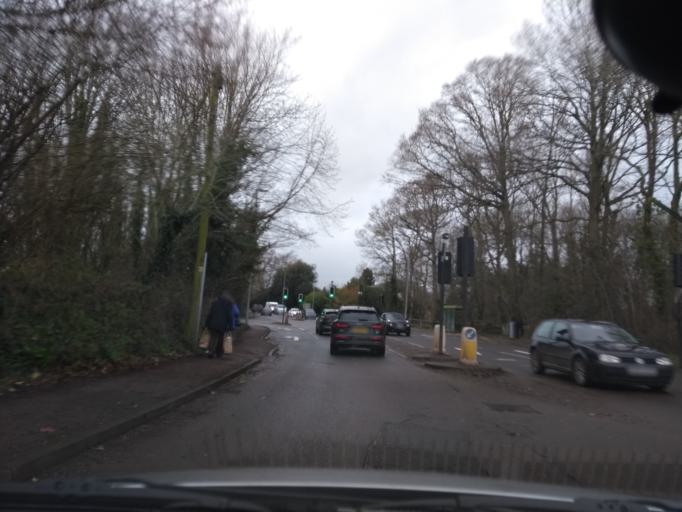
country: GB
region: England
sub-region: Somerset
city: Taunton
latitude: 51.0301
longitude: -3.1271
